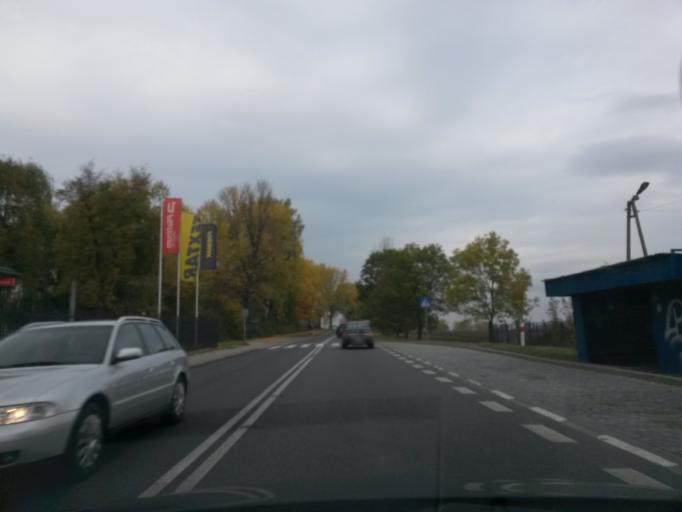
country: PL
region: Lower Silesian Voivodeship
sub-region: Powiat dzierzoniowski
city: Niemcza
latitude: 50.6958
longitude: 16.8220
